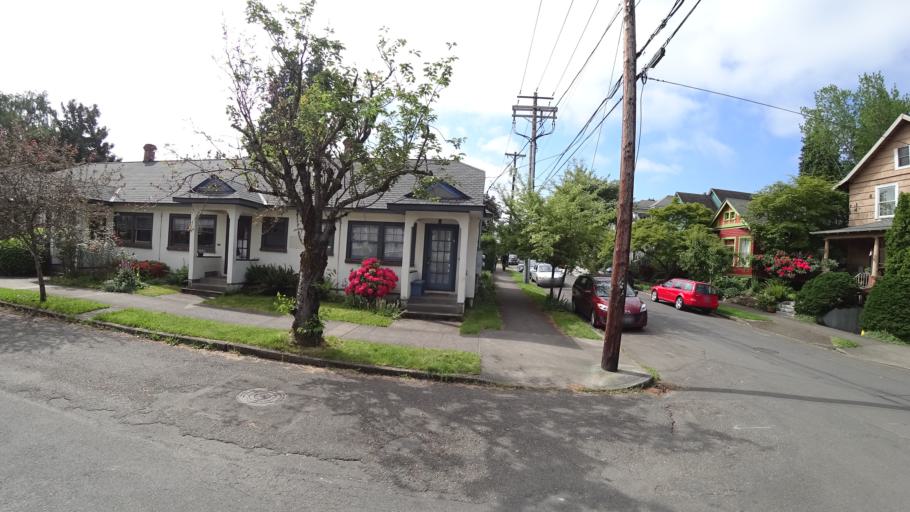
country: US
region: Oregon
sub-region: Multnomah County
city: Portland
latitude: 45.5157
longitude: -122.6322
